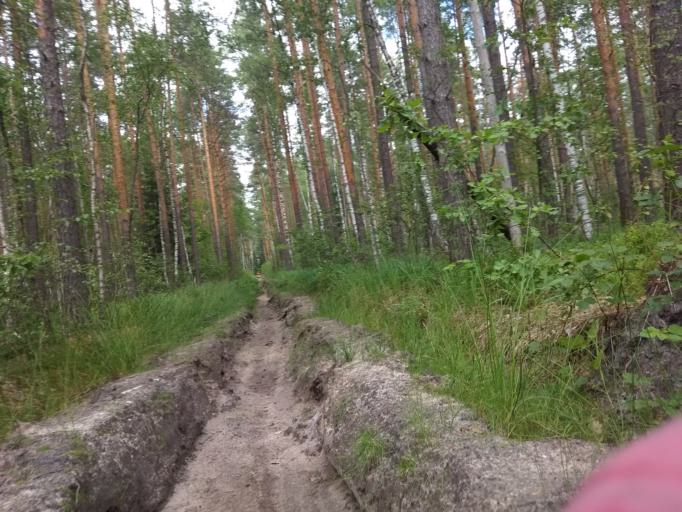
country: RU
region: Moskovskaya
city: Misheronskiy
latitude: 55.6836
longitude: 39.7096
